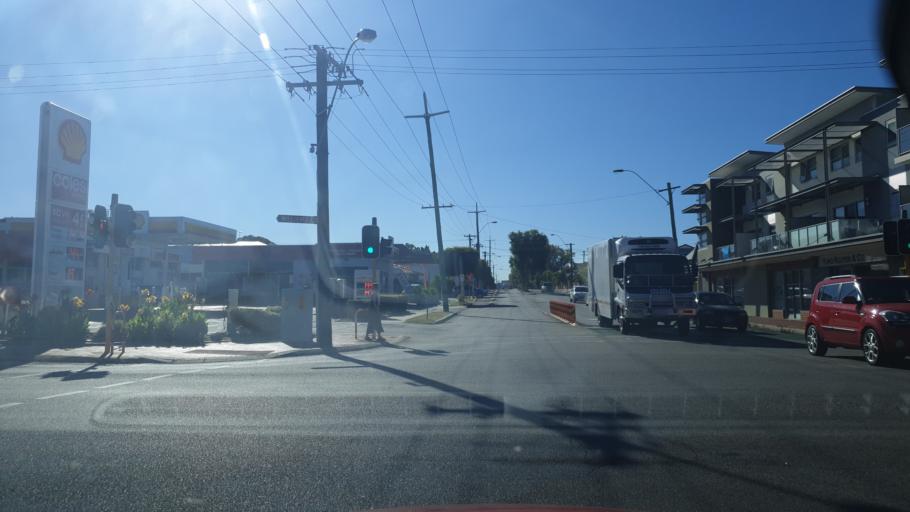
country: AU
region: Western Australia
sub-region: Vincent
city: Mount Lawley
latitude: -31.9409
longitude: 115.8636
